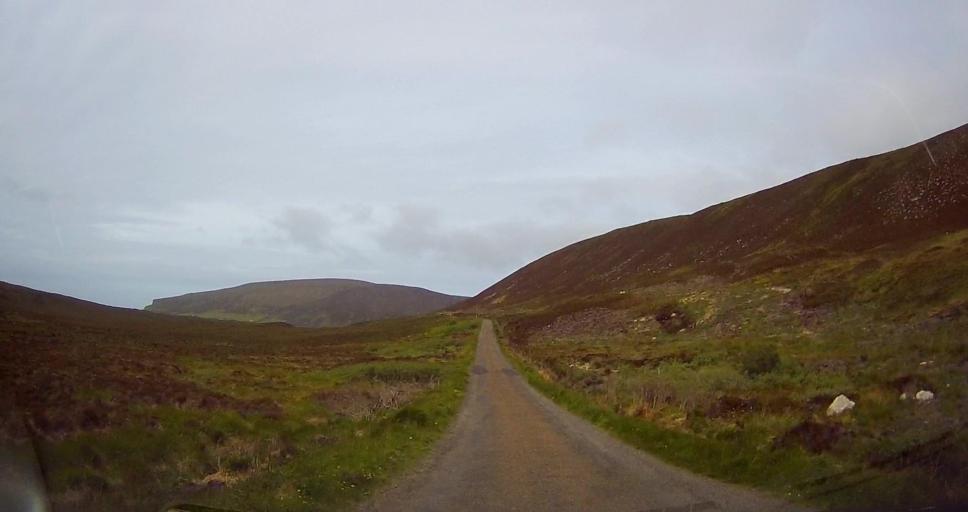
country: GB
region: Scotland
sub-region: Orkney Islands
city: Stromness
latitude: 58.8816
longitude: -3.3501
